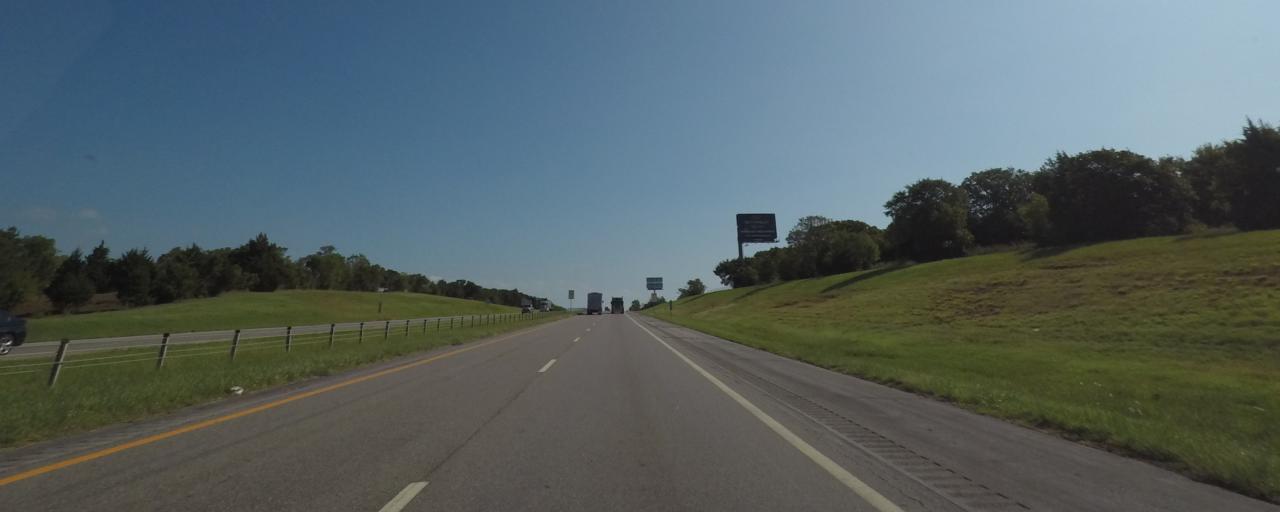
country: US
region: Oklahoma
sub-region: Logan County
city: Guthrie
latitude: 35.8277
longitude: -97.4061
